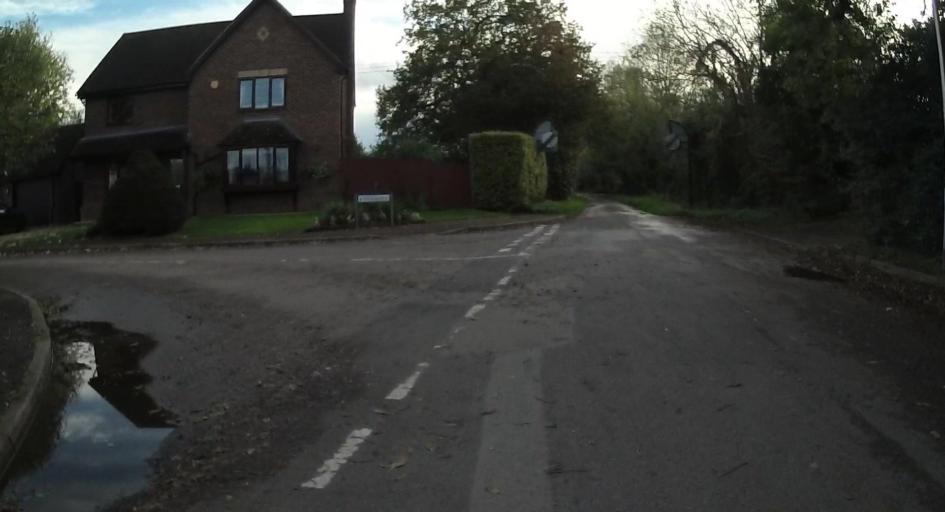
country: GB
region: England
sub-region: Wokingham
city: Swallowfield
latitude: 51.3760
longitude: -0.9598
